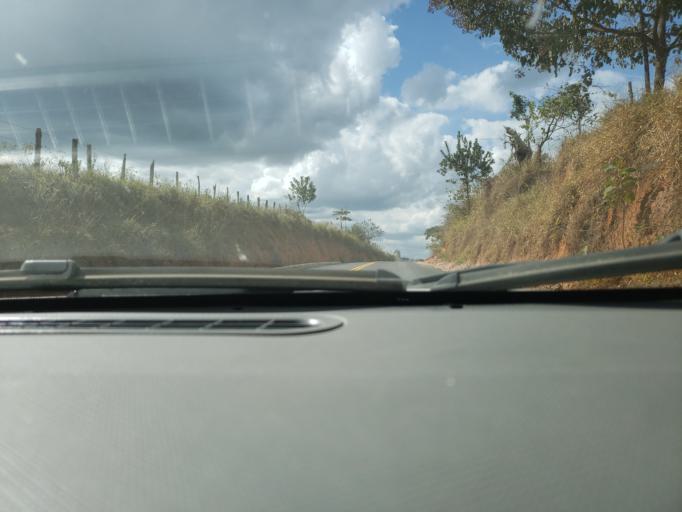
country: BR
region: Minas Gerais
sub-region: Campo Belo
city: Campo Belo
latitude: -20.9087
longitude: -45.2907
